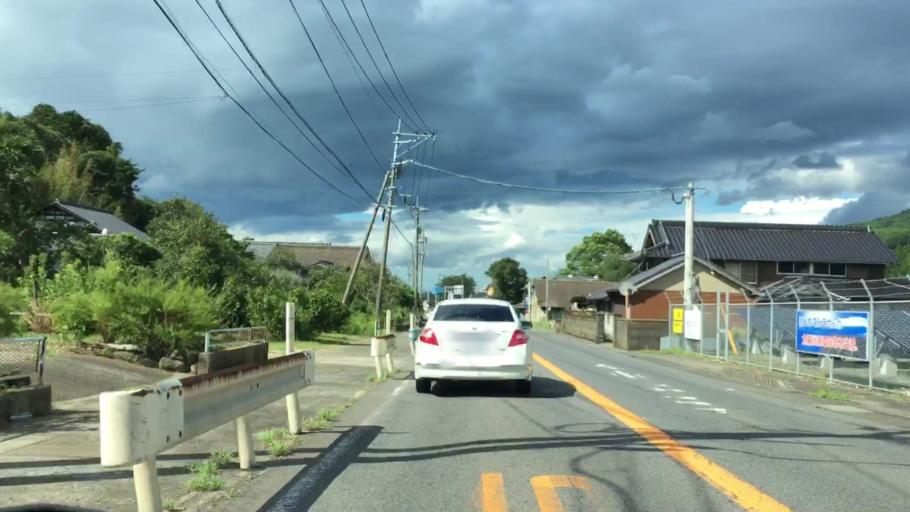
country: JP
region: Saga Prefecture
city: Imaricho-ko
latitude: 33.2305
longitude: 129.8490
